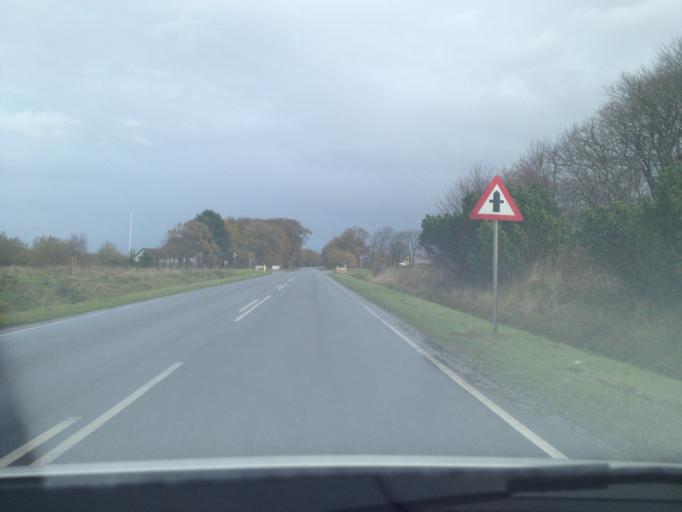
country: DK
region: South Denmark
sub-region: Tonder Kommune
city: Sherrebek
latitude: 55.0608
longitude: 8.8117
